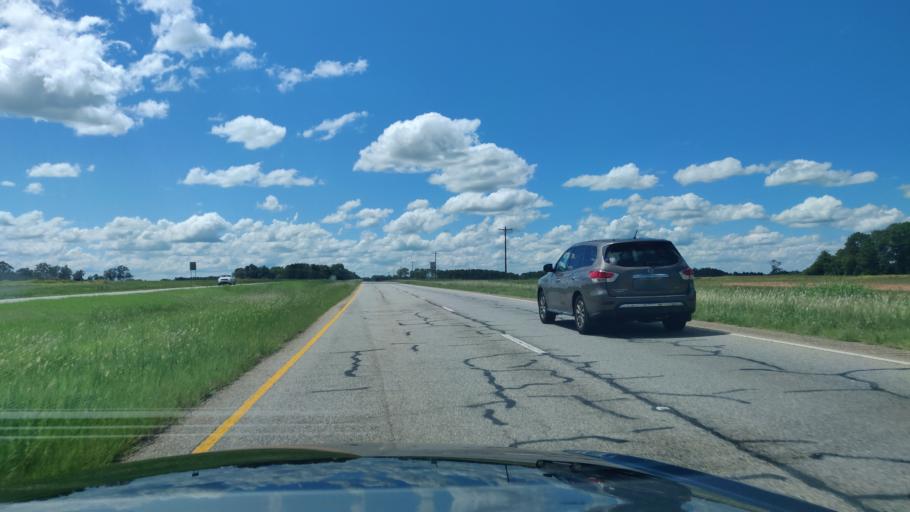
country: US
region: Georgia
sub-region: Stewart County
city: Richland
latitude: 31.9872
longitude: -84.6292
